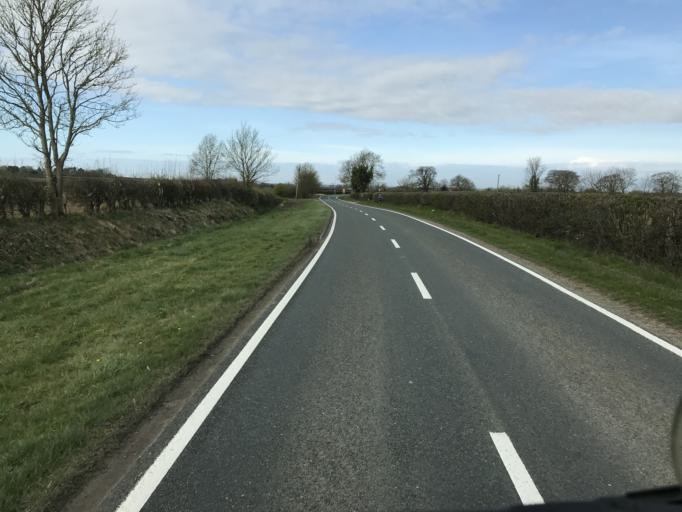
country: GB
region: England
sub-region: Lincolnshire
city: Market Rasen
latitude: 53.3868
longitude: -0.3934
